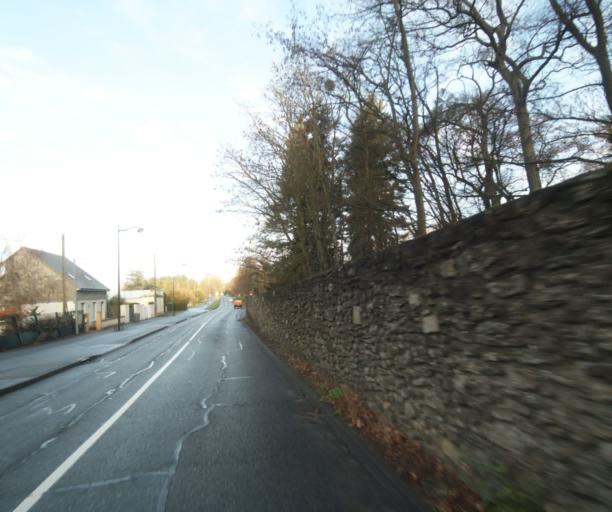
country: FR
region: Pays de la Loire
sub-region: Departement de la Sarthe
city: Change
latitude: 47.9890
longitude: 0.2417
